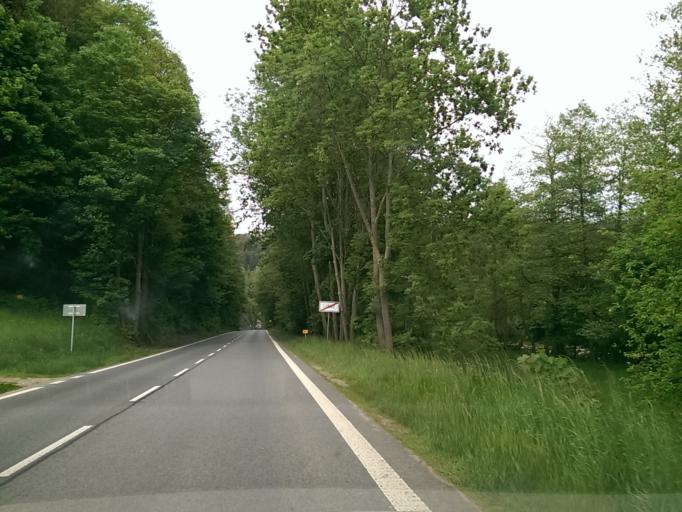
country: CZ
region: Liberecky
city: Mala Skala
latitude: 50.6503
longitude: 15.2111
